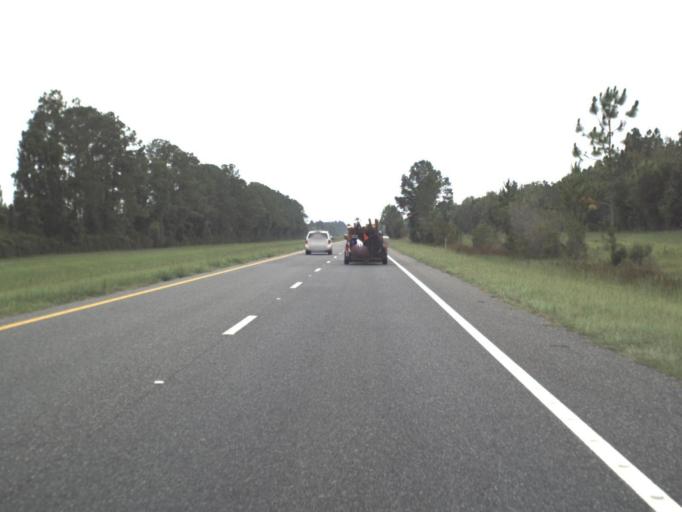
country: US
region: Florida
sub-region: Levy County
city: Bronson
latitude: 29.3100
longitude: -82.7578
